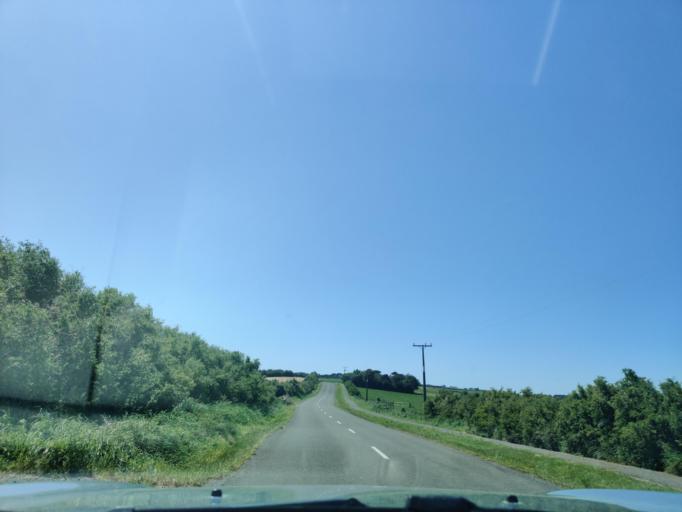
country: NZ
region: Taranaki
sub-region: South Taranaki District
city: Hawera
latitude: -39.6027
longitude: 174.2471
